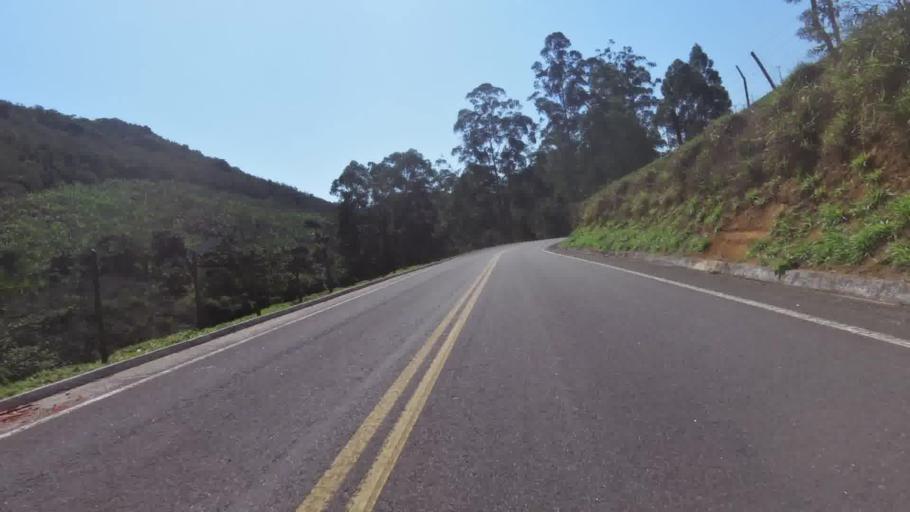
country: BR
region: Espirito Santo
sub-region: Alfredo Chaves
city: Alfredo Chaves
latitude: -20.5662
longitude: -40.8064
